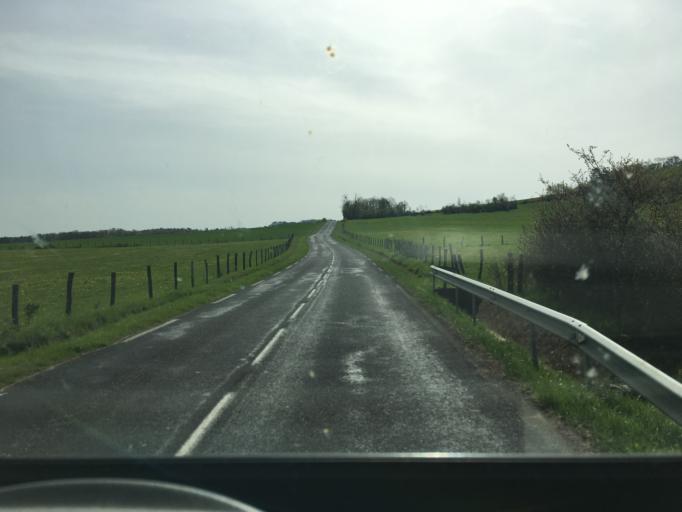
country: FR
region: Lorraine
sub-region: Departement de Meurthe-et-Moselle
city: Gondreville
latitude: 48.6679
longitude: 5.9444
